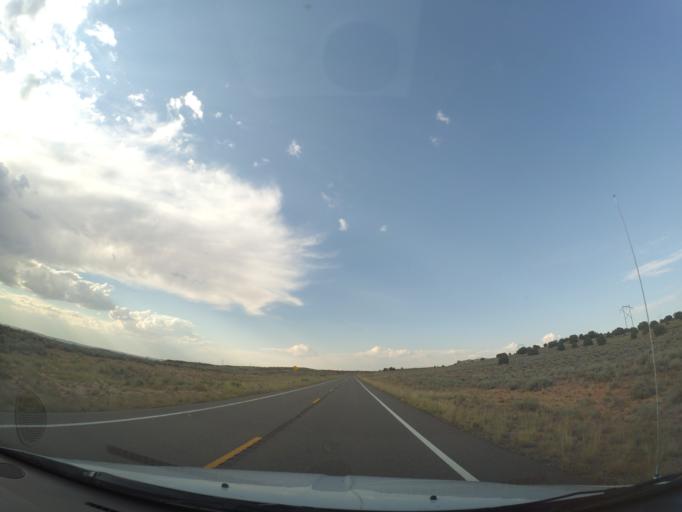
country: US
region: Arizona
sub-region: Coconino County
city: LeChee
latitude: 36.6899
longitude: -111.4444
